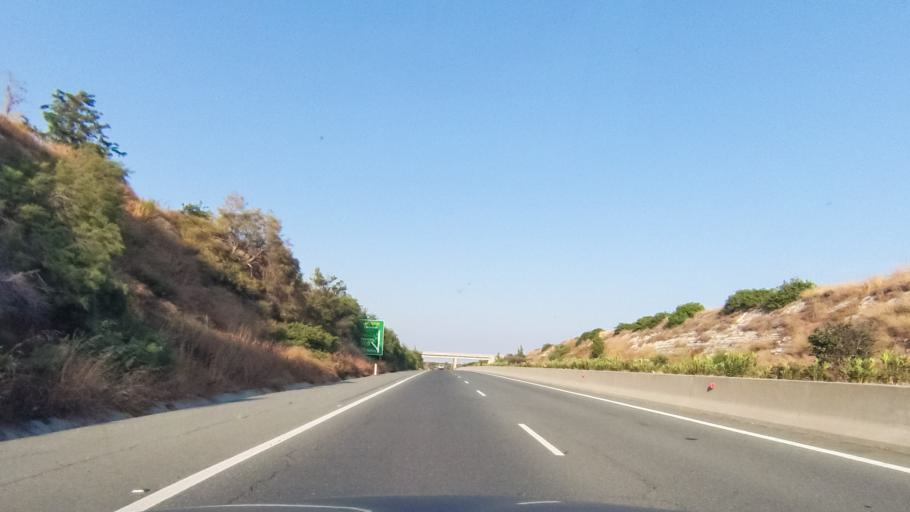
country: CY
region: Limassol
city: Erimi
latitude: 34.6902
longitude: 32.9334
